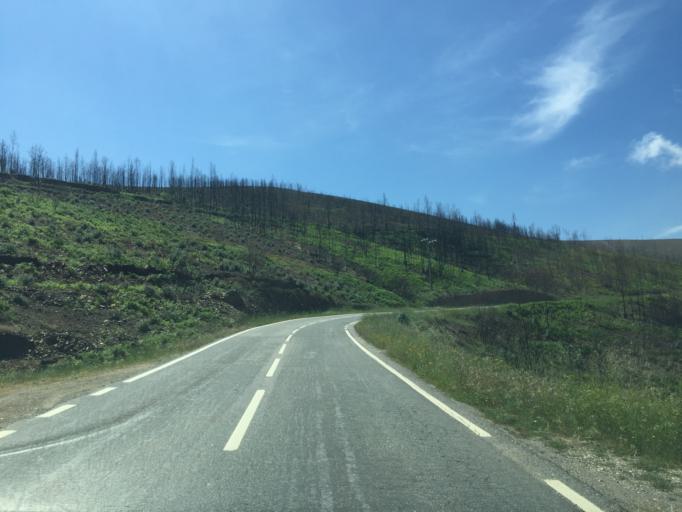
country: PT
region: Coimbra
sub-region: Pampilhosa da Serra
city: Pampilhosa da Serra
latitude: 40.0394
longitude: -7.9584
